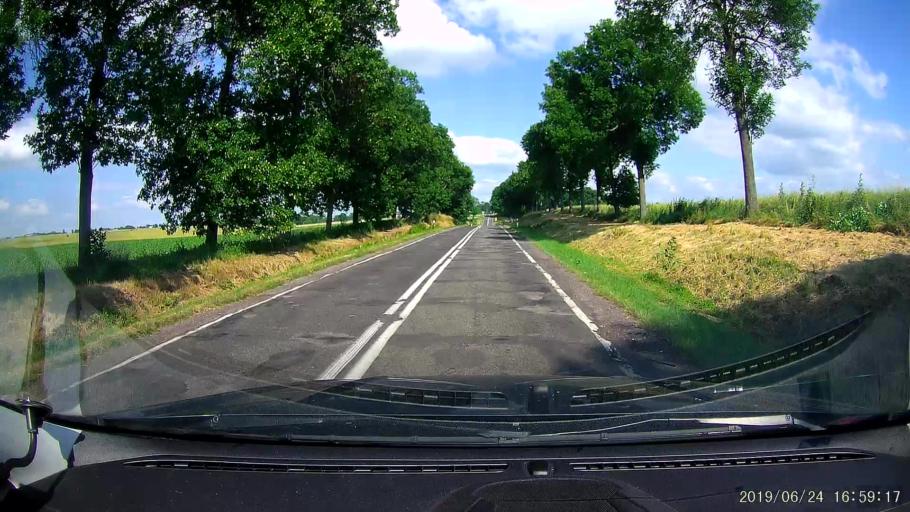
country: PL
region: Lublin Voivodeship
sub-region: Powiat tomaszowski
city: Telatyn
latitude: 50.5238
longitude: 23.8988
